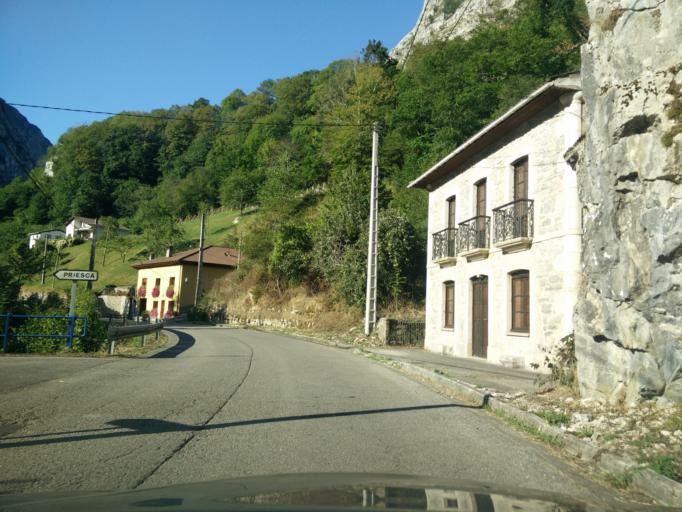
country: ES
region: Asturias
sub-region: Province of Asturias
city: Parres
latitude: 43.2520
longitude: -5.2002
